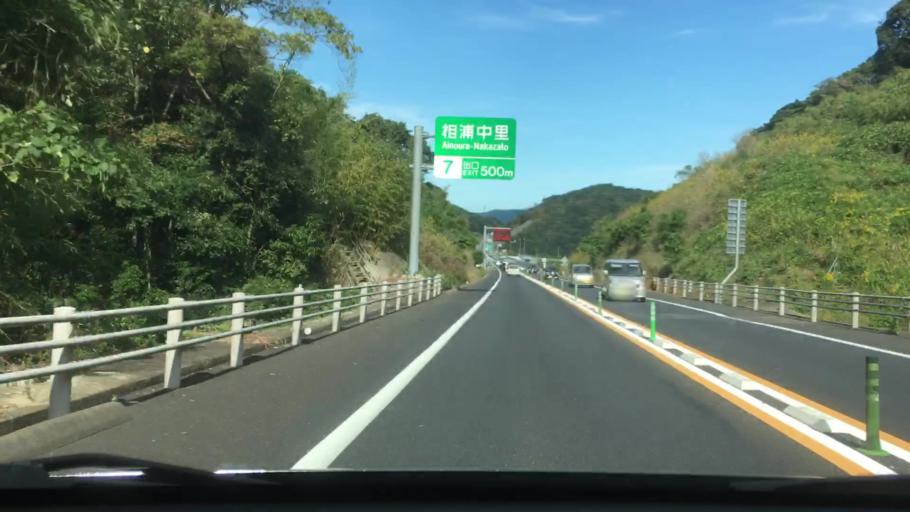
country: JP
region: Nagasaki
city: Sasebo
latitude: 33.1974
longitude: 129.6773
